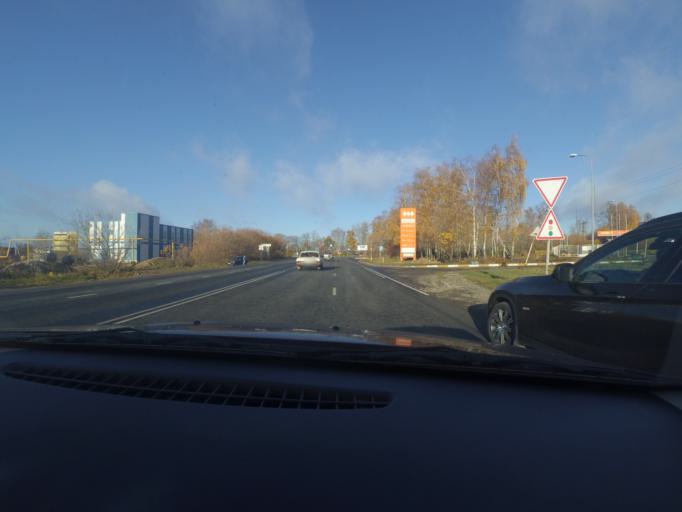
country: RU
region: Nizjnij Novgorod
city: Nizhniy Novgorod
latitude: 56.2185
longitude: 43.9388
